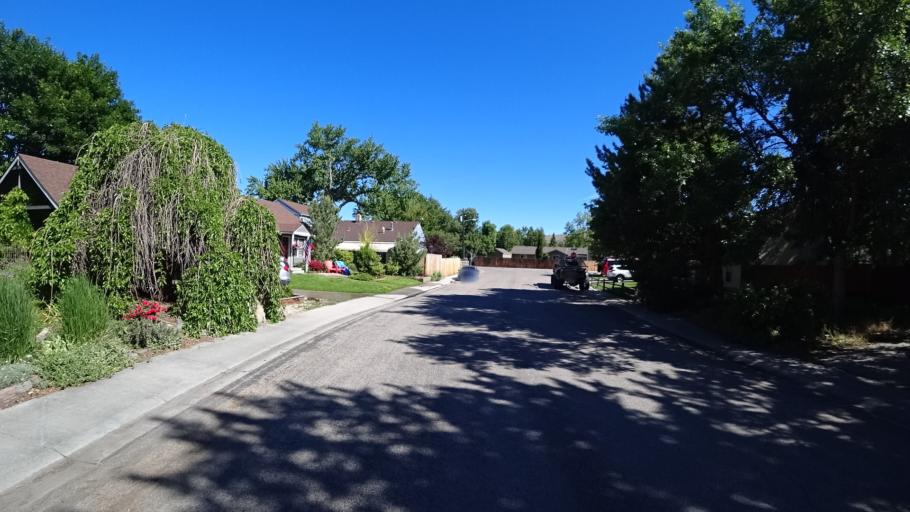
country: US
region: Idaho
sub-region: Ada County
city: Garden City
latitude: 43.6643
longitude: -116.2618
